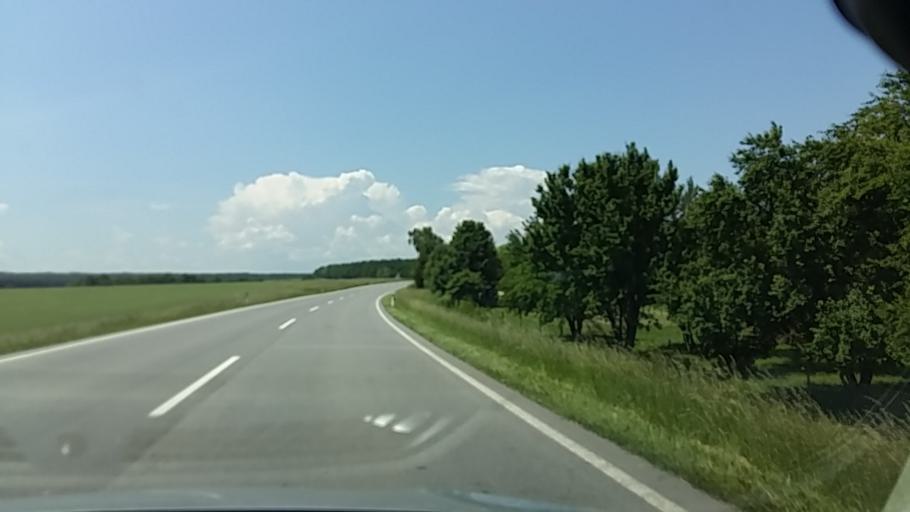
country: AT
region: Burgenland
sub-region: Politischer Bezirk Oberpullendorf
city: Raiding
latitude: 47.5338
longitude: 16.5382
